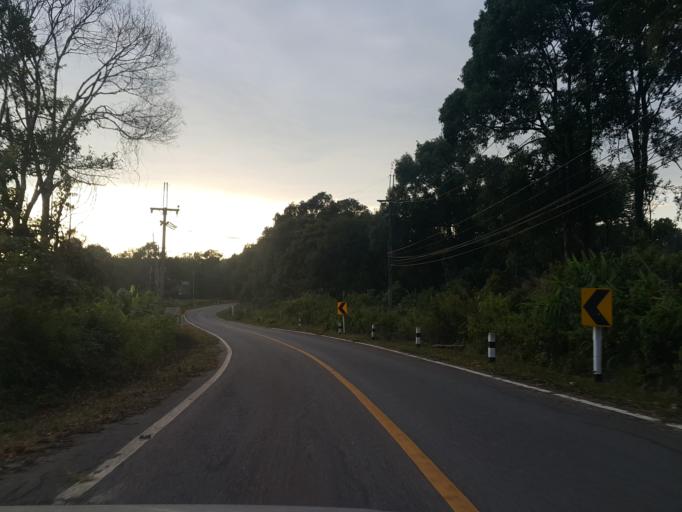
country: TH
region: Mae Hong Son
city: Khun Yuam
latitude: 18.8010
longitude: 98.0636
